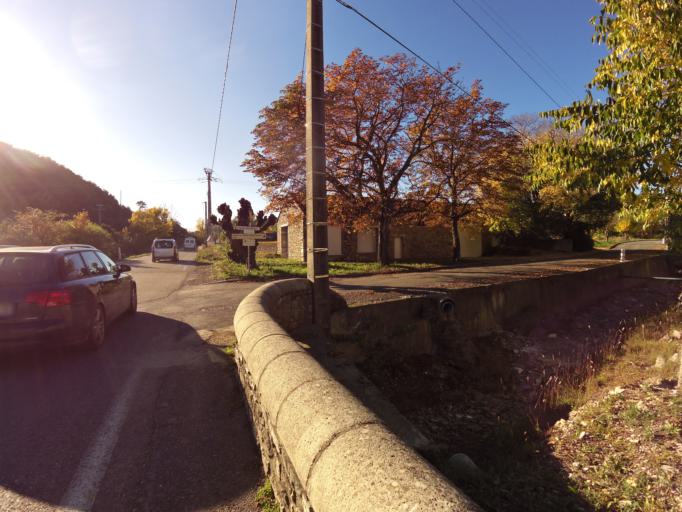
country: FR
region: Languedoc-Roussillon
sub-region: Departement du Gard
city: Sauve
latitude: 43.9890
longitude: 3.9508
